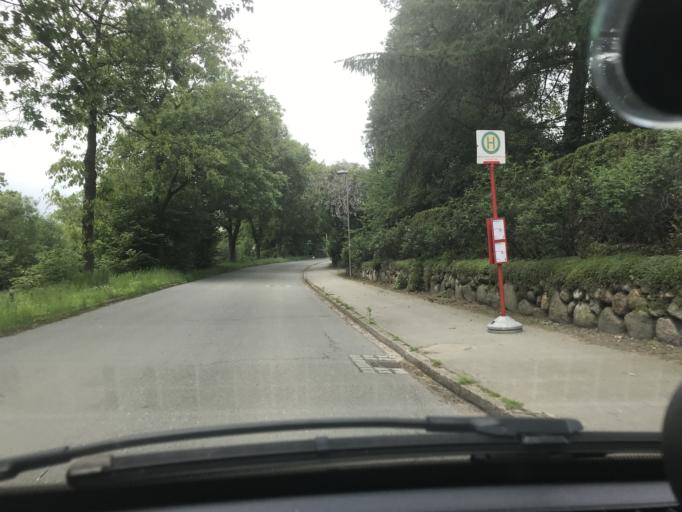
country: DE
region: Schleswig-Holstein
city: Rausdorf
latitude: 53.5893
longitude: 10.3309
